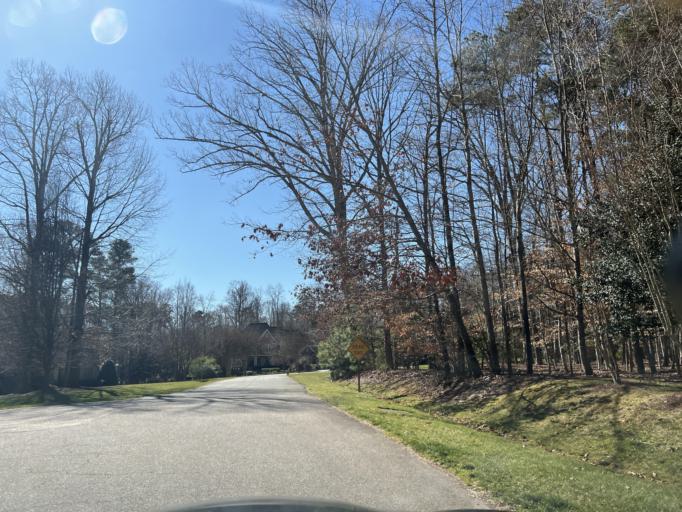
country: US
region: North Carolina
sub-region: Wake County
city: West Raleigh
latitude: 35.9035
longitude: -78.6183
